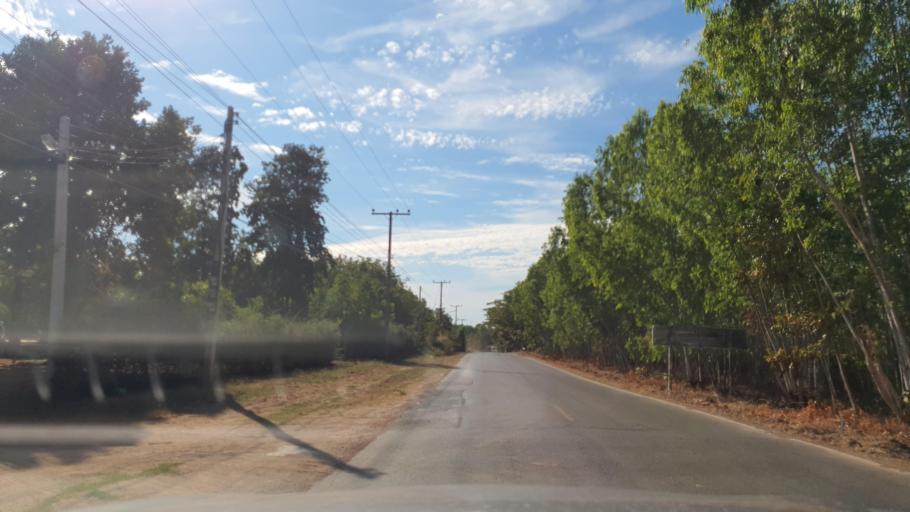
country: TH
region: Kalasin
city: Kuchinarai
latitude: 16.5420
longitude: 104.0874
